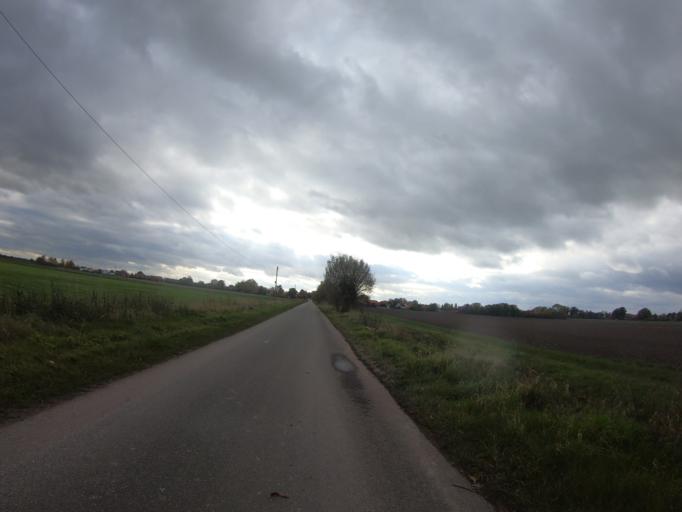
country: DE
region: Lower Saxony
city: Adenbuettel
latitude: 52.3836
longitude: 10.4850
